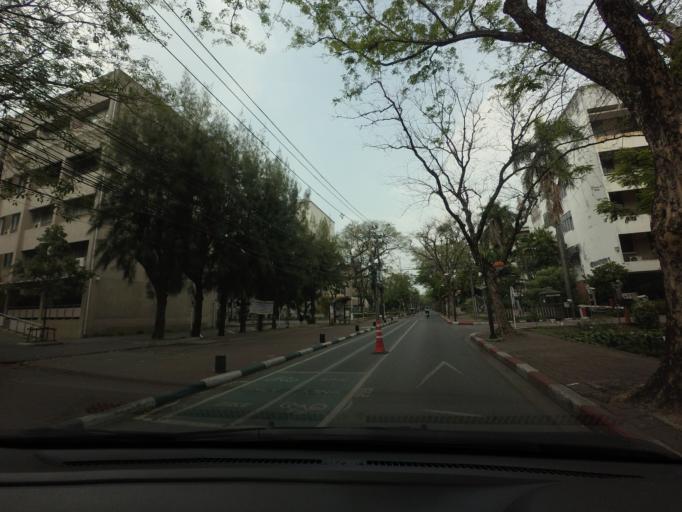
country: TH
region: Bangkok
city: Chatuchak
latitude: 13.8486
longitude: 100.5706
